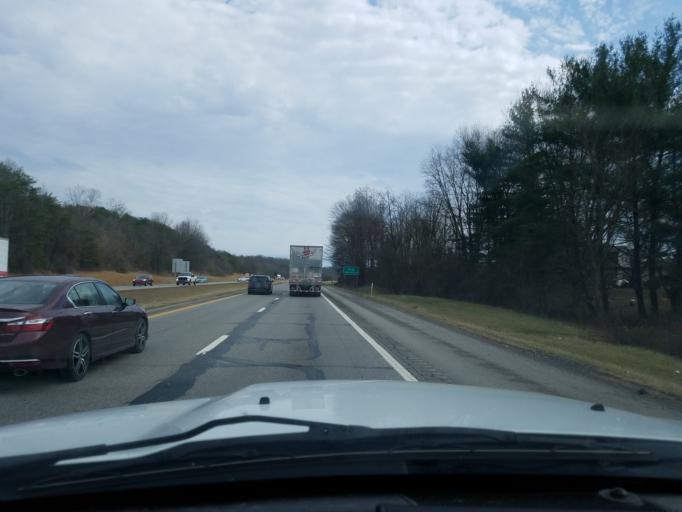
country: US
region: West Virginia
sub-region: Kanawha County
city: Nitro
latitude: 38.4550
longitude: -81.8743
